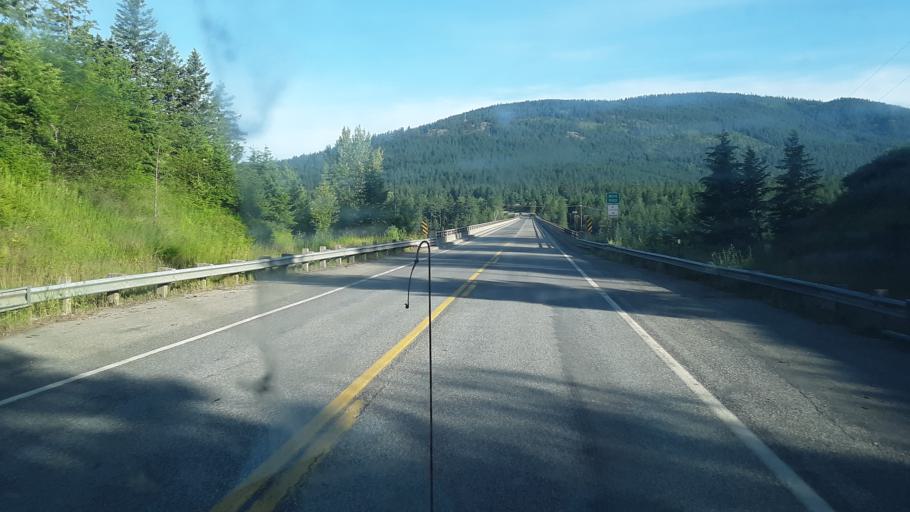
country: US
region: Idaho
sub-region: Boundary County
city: Bonners Ferry
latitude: 48.7272
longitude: -116.1759
